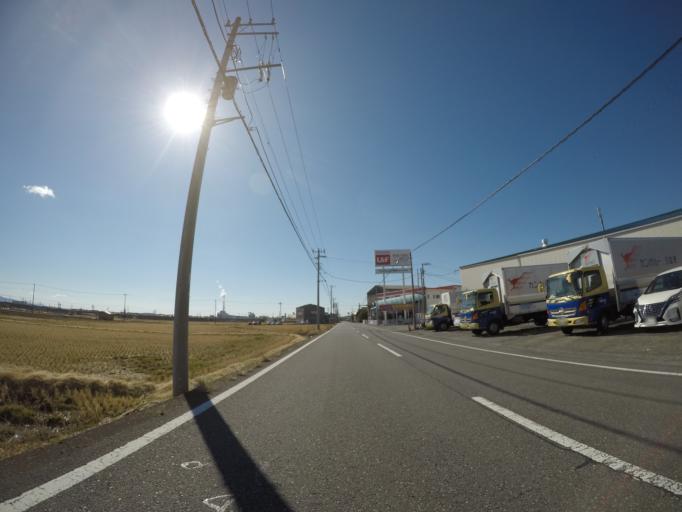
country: JP
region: Shizuoka
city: Fuji
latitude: 35.1570
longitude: 138.7219
